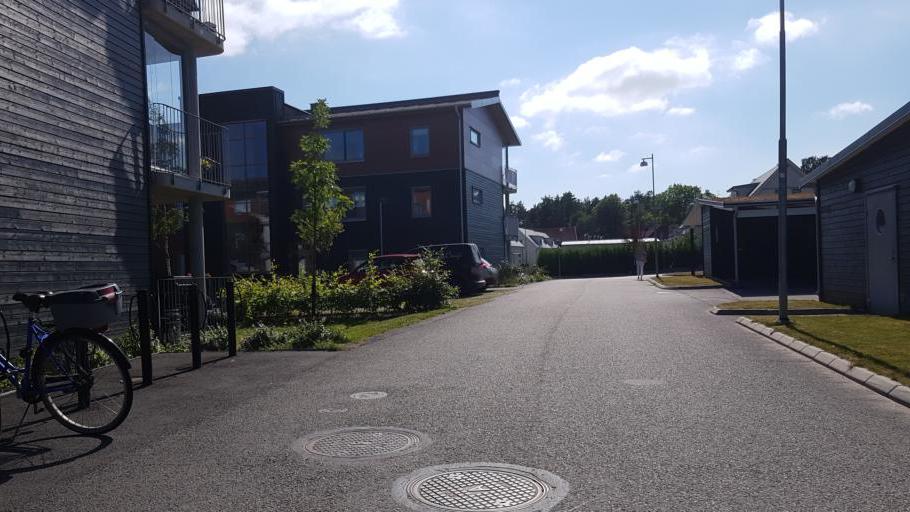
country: SE
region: Vaestra Goetaland
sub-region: Partille Kommun
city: Ojersjo
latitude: 57.6878
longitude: 12.1124
